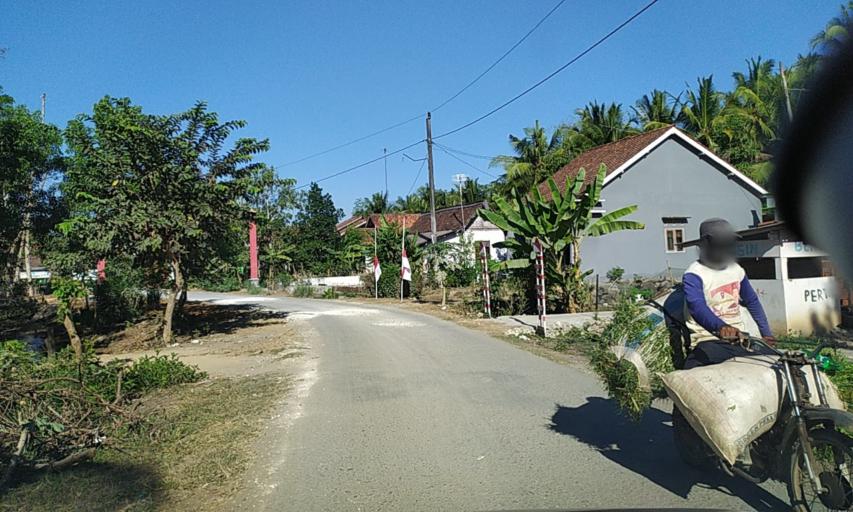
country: ID
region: Central Java
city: Kalenaren
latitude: -7.5808
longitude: 108.7982
